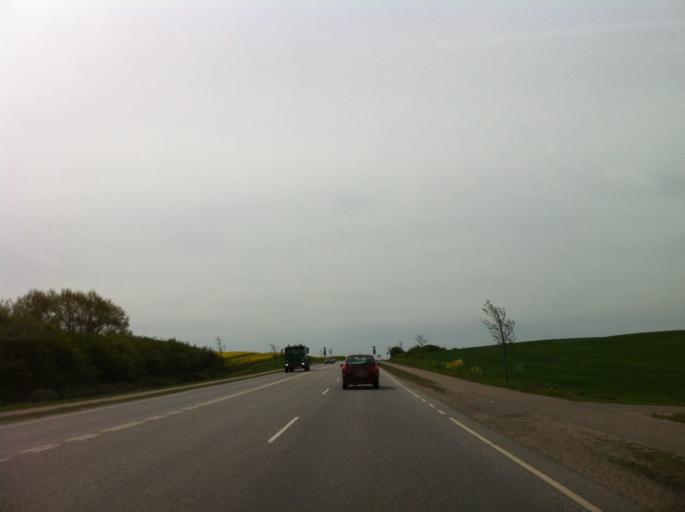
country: DK
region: Zealand
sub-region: Roskilde Kommune
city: Gundsomagle
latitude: 55.7264
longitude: 12.1216
